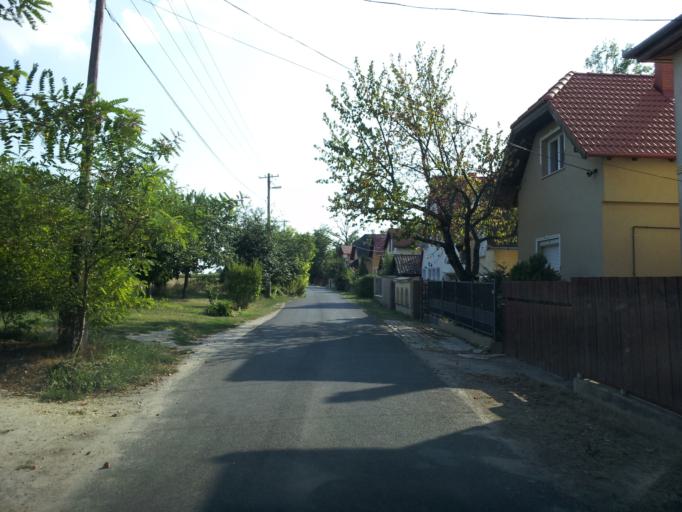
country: HU
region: Pest
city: Szigethalom
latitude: 47.3013
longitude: 19.0281
